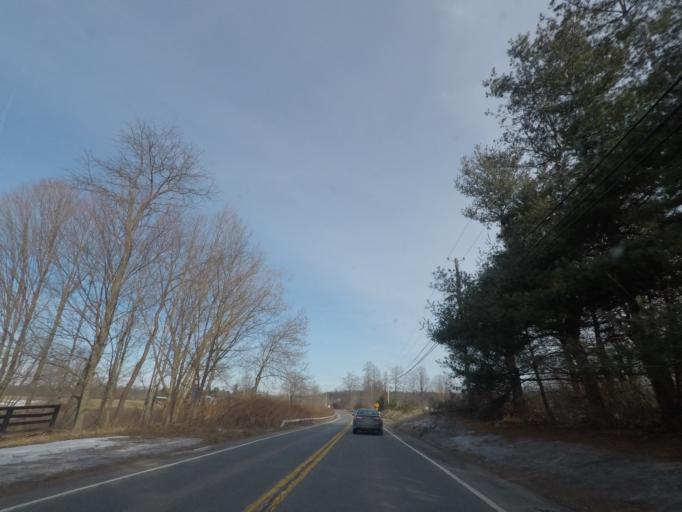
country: US
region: New York
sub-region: Columbia County
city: Niverville
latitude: 42.4639
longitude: -73.6380
